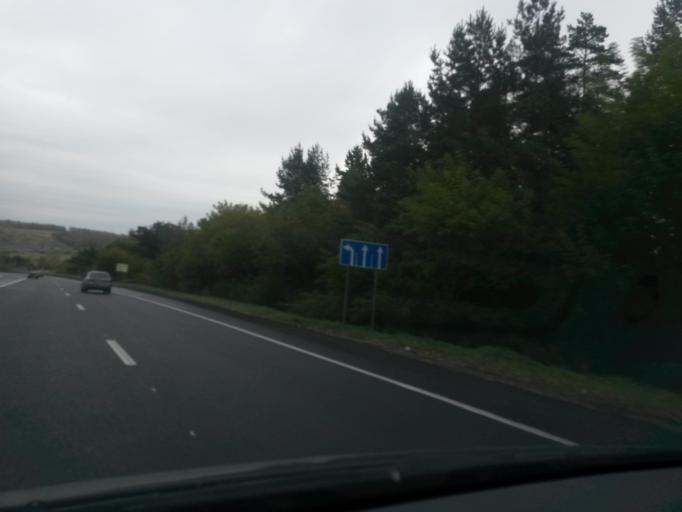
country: RU
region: Nizjnij Novgorod
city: Pamyat' Parizhskoy Kommuny
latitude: 56.0273
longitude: 44.5998
